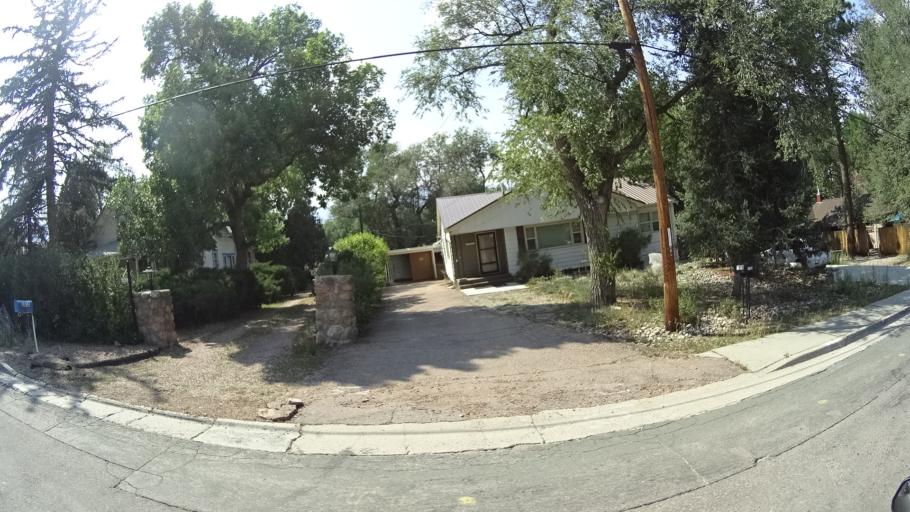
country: US
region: Colorado
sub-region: El Paso County
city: Colorado Springs
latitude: 38.8046
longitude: -104.8282
